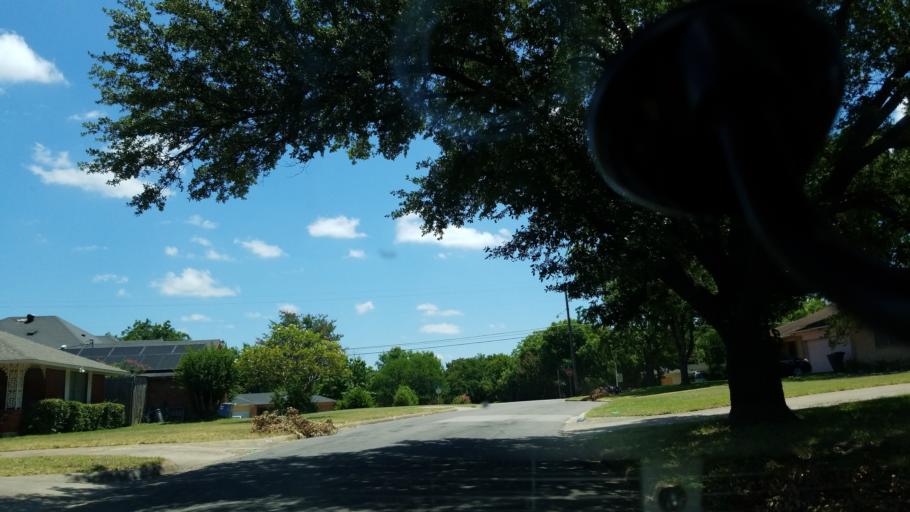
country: US
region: Texas
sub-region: Dallas County
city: Cockrell Hill
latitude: 32.6806
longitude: -96.8154
